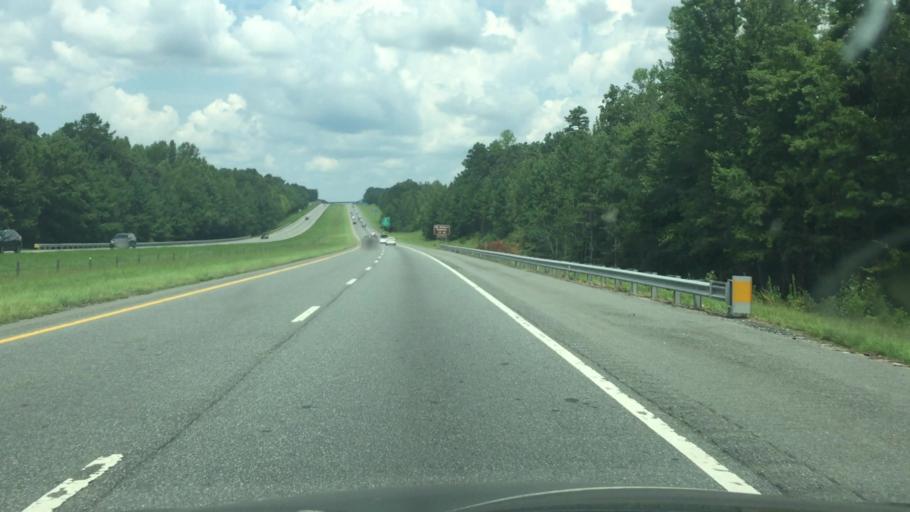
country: US
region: North Carolina
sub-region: Montgomery County
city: Biscoe
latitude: 35.5212
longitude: -79.7831
